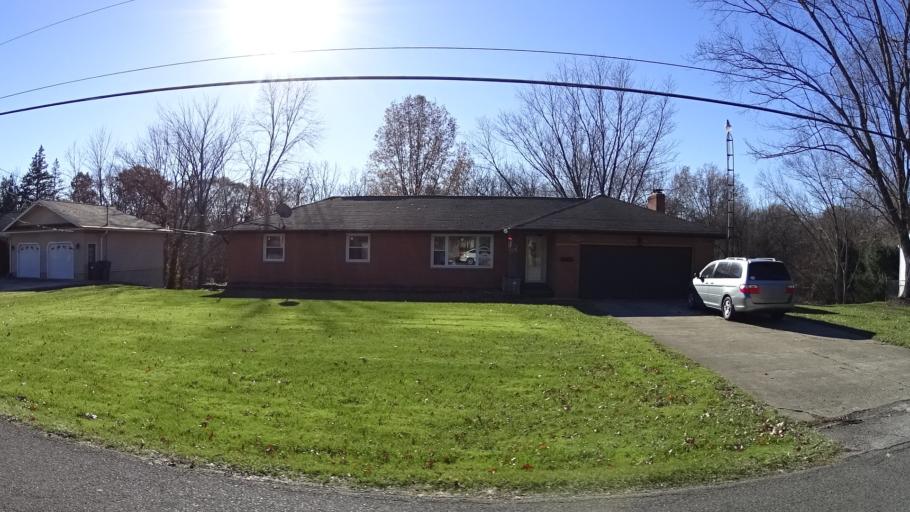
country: US
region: Ohio
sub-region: Lorain County
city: Elyria
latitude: 41.3344
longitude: -82.0714
